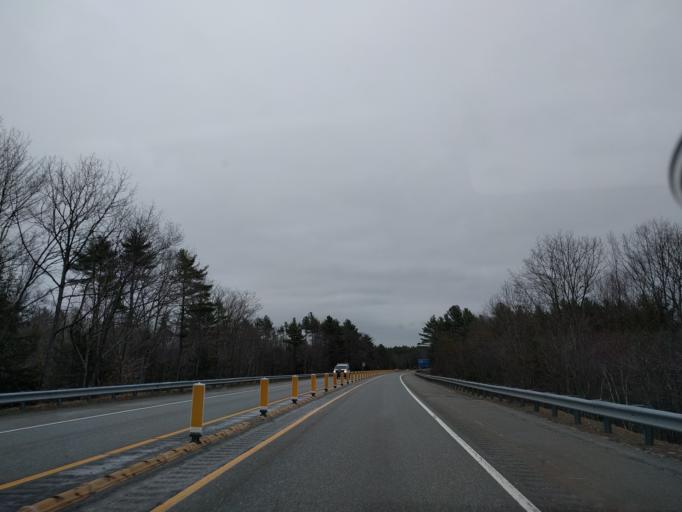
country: US
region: Massachusetts
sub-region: Worcester County
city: Phillipston
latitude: 42.5727
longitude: -72.1443
